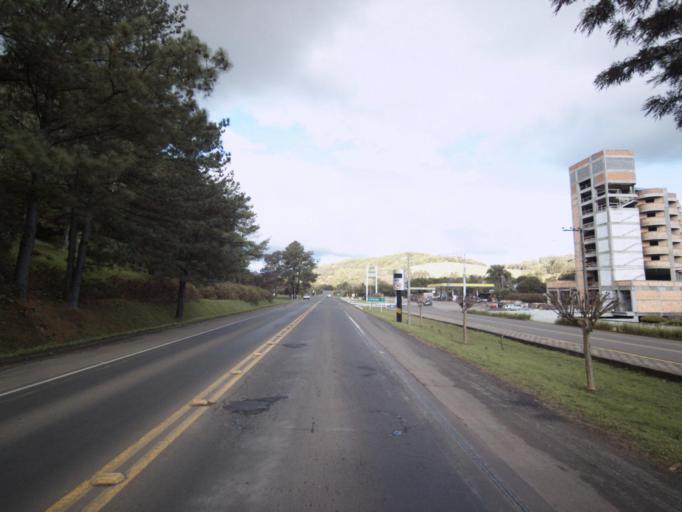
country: BR
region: Santa Catarina
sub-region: Joacaba
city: Joacaba
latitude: -27.2837
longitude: -51.4352
